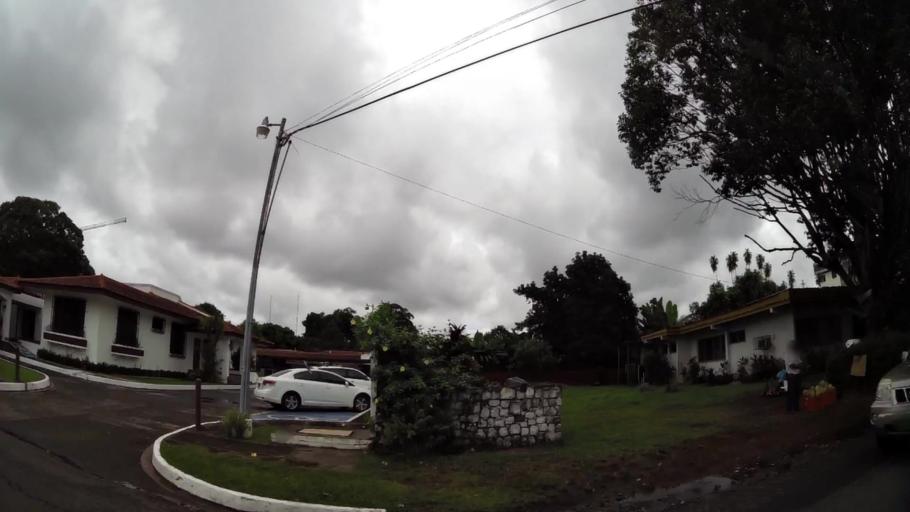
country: PA
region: Chiriqui
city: David
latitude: 8.4329
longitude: -82.4262
